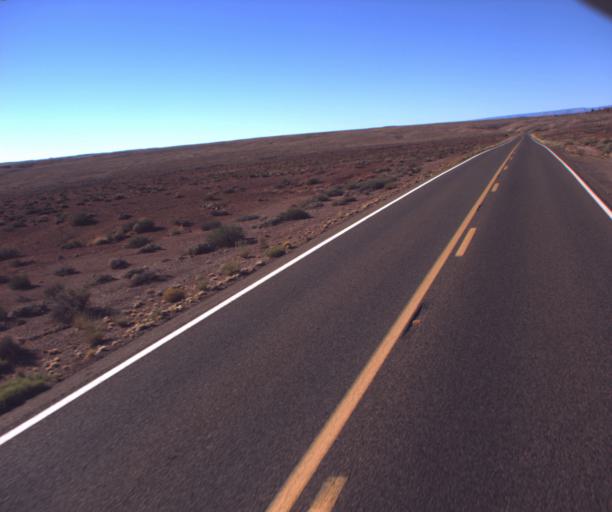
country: US
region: Arizona
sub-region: Coconino County
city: Page
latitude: 36.7737
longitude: -111.6986
